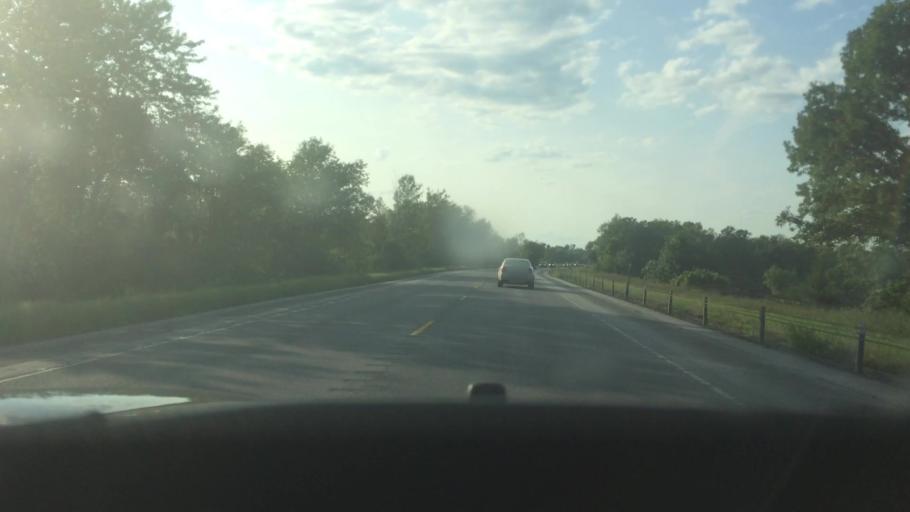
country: US
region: New York
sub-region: St. Lawrence County
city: Canton
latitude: 44.6122
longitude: -75.2149
